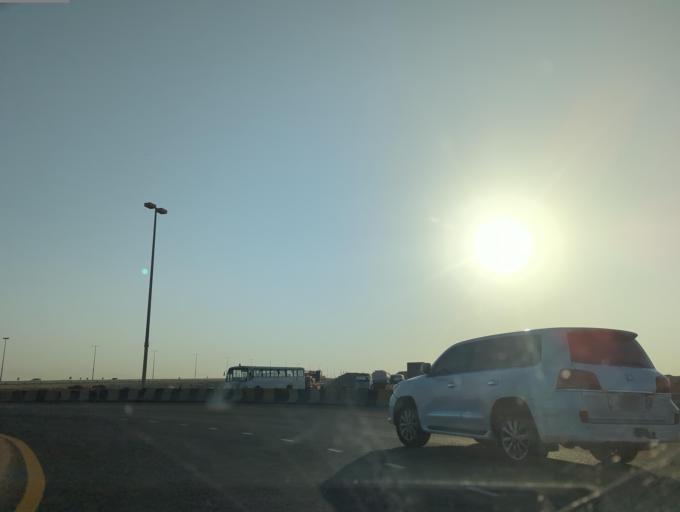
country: AE
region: Abu Dhabi
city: Abu Dhabi
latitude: 24.4631
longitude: 54.6808
